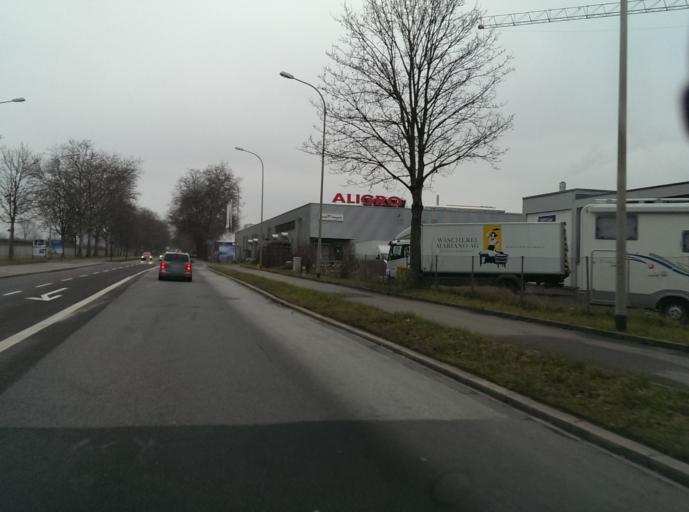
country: CH
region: Zurich
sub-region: Bezirk Dietikon
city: Oberengstringen / Zentrum
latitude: 47.4004
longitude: 8.4650
